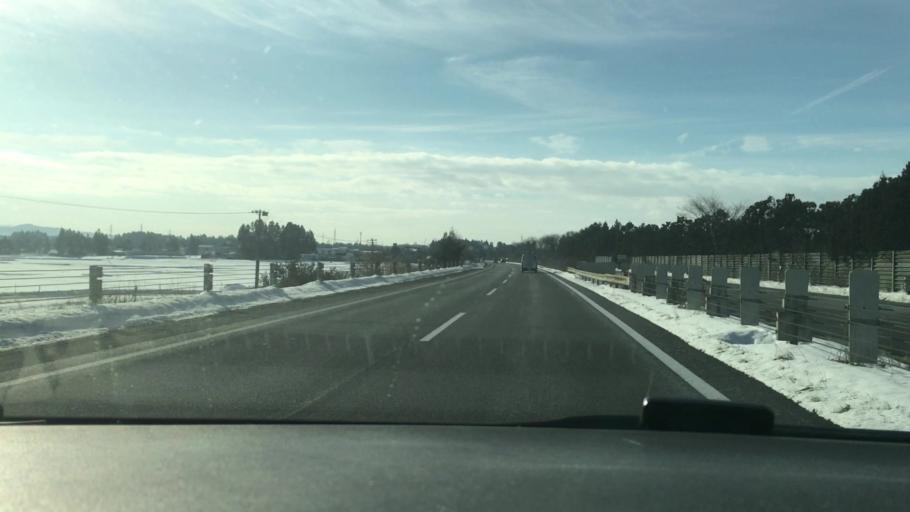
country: JP
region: Iwate
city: Hanamaki
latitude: 39.3580
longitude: 141.0895
